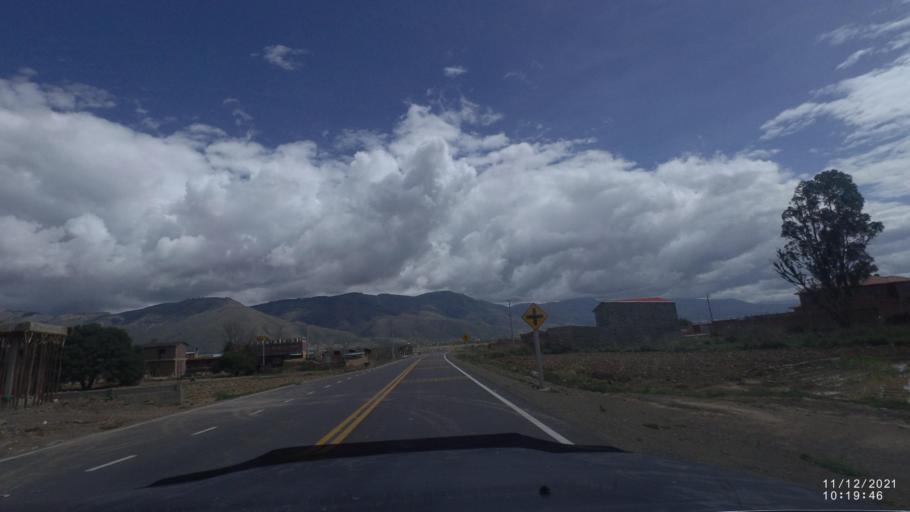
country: BO
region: Cochabamba
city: Tarata
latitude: -17.5652
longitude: -66.0085
